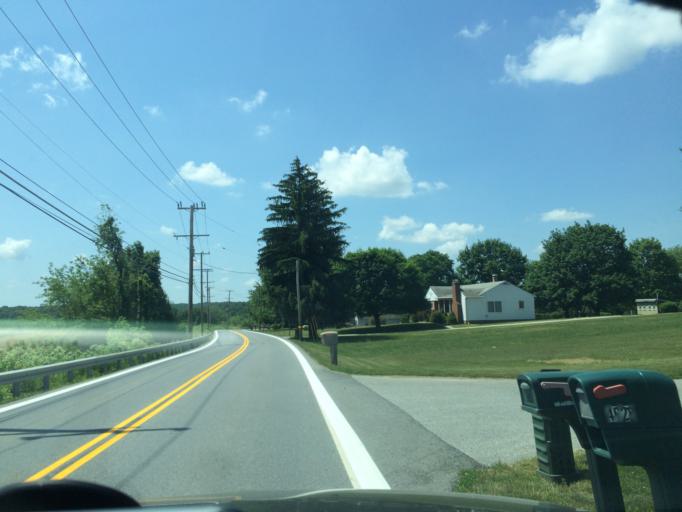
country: US
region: Maryland
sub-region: Carroll County
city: Eldersburg
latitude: 39.4472
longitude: -76.9253
